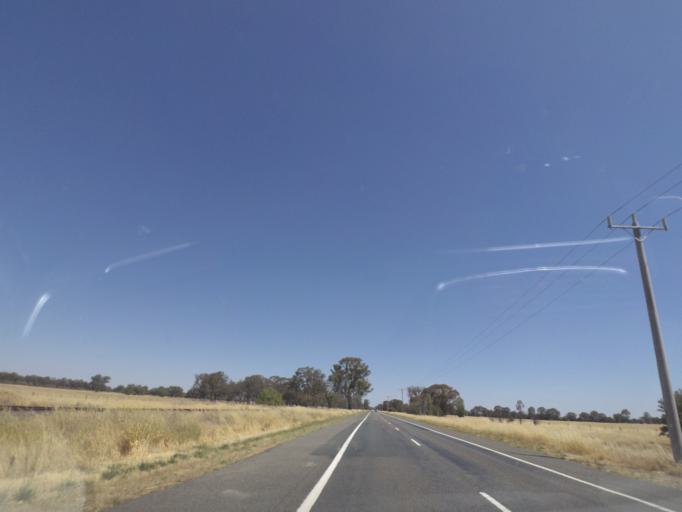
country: AU
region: Victoria
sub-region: Greater Shepparton
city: Shepparton
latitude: -36.2080
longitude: 145.4319
